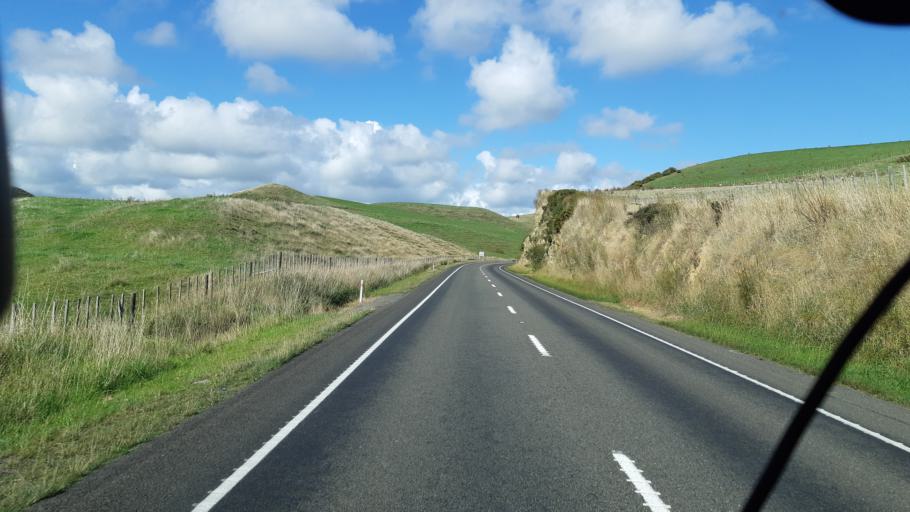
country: NZ
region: Manawatu-Wanganui
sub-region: Wanganui District
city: Wanganui
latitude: -40.0174
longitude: 175.1753
